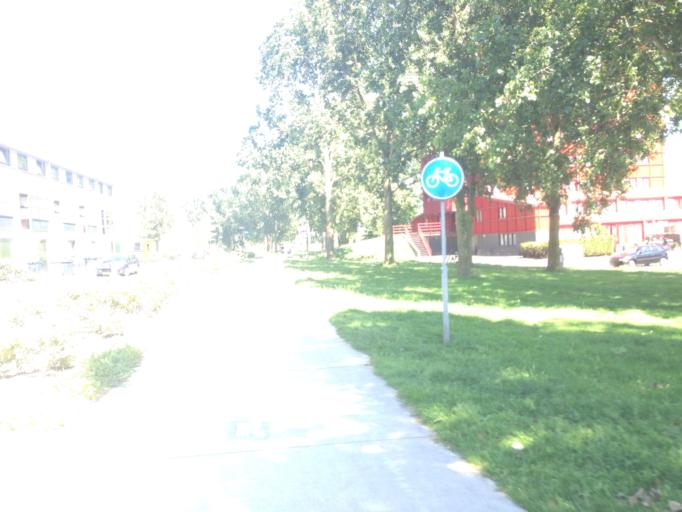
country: NL
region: Flevoland
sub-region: Gemeente Almere
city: Almere Stad
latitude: 52.3916
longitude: 5.3033
